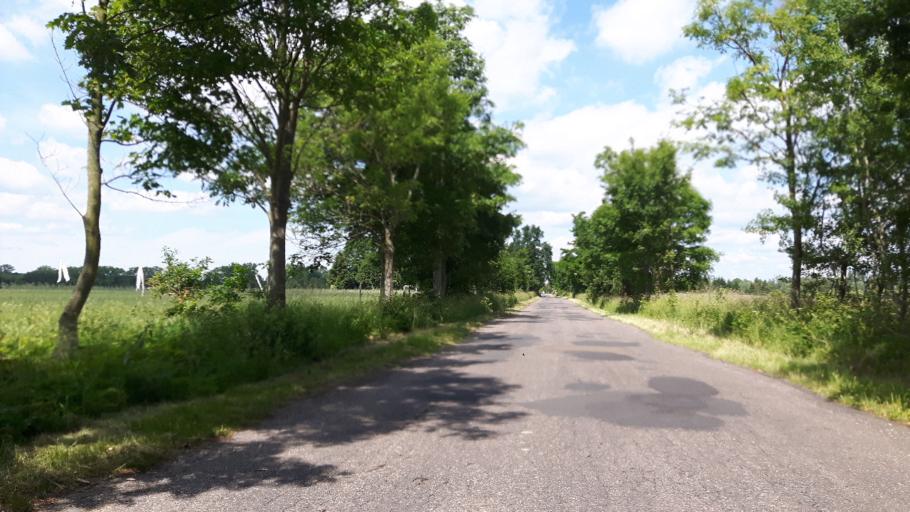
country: PL
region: West Pomeranian Voivodeship
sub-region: Powiat goleniowski
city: Osina
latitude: 53.6733
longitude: 14.9988
